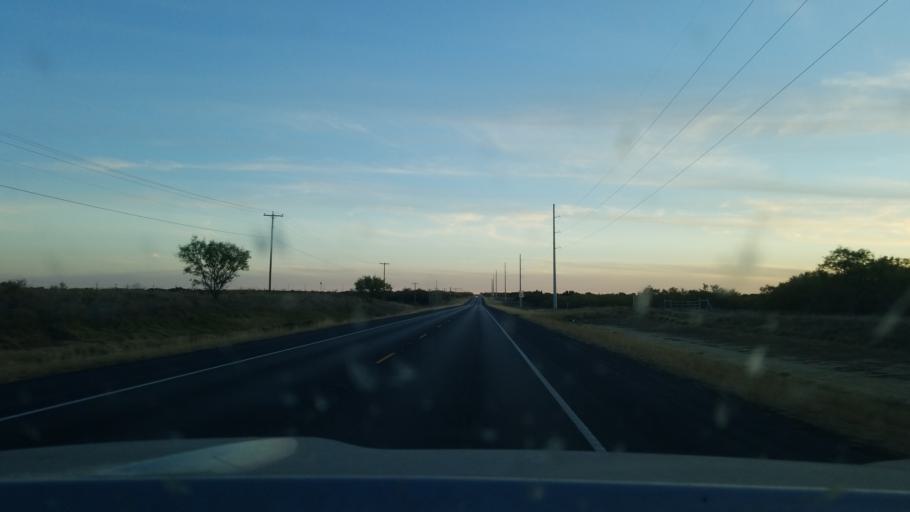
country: US
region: Texas
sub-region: Stephens County
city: Breckenridge
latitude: 32.7074
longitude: -98.9027
